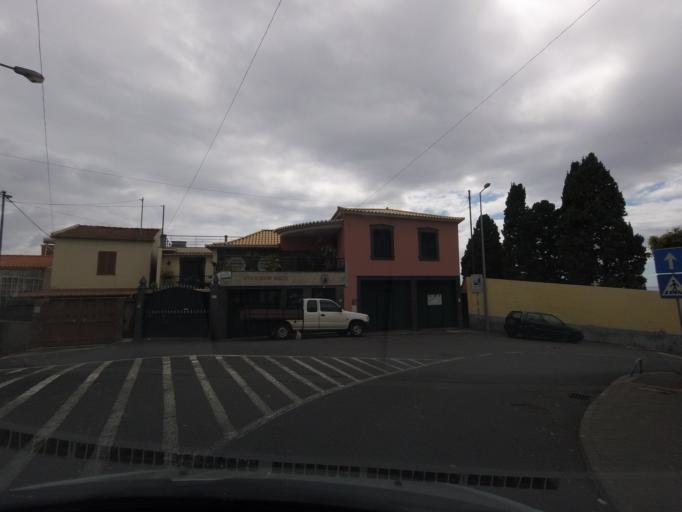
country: PT
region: Madeira
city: Camara de Lobos
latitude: 32.6475
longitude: -16.9705
